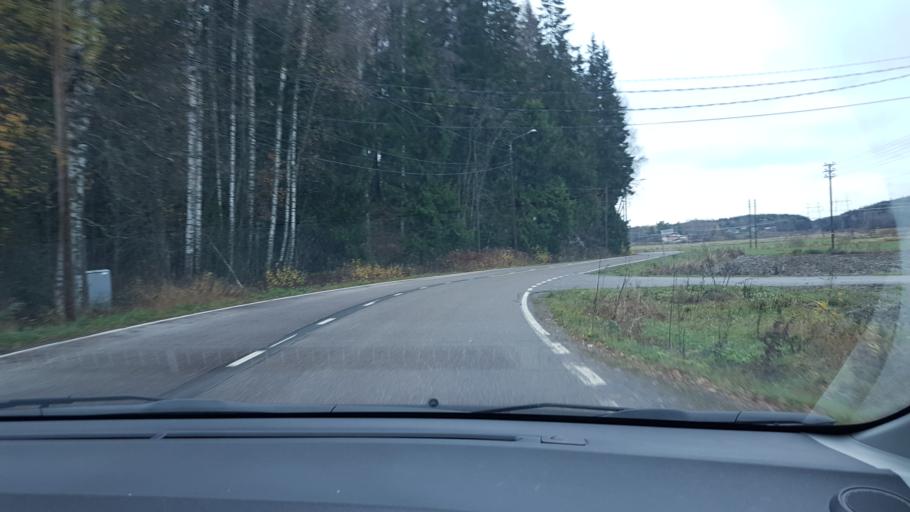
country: FI
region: Uusimaa
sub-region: Helsinki
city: Vantaa
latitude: 60.2733
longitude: 25.1383
